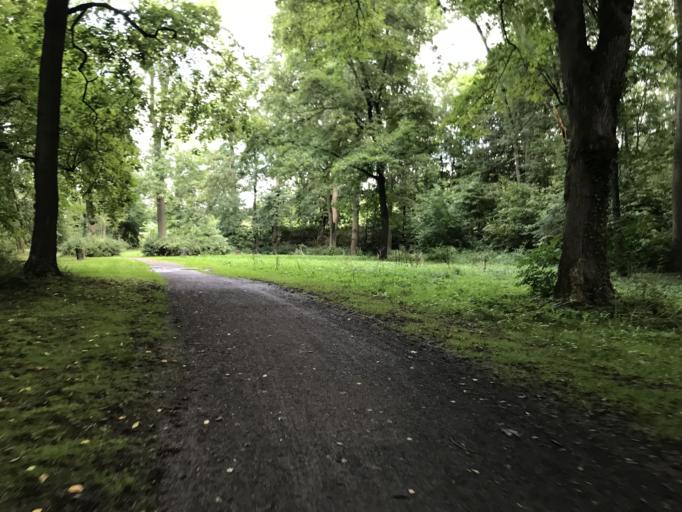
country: DE
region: Hesse
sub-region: Regierungsbezirk Giessen
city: Alsfeld
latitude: 50.7439
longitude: 9.2773
